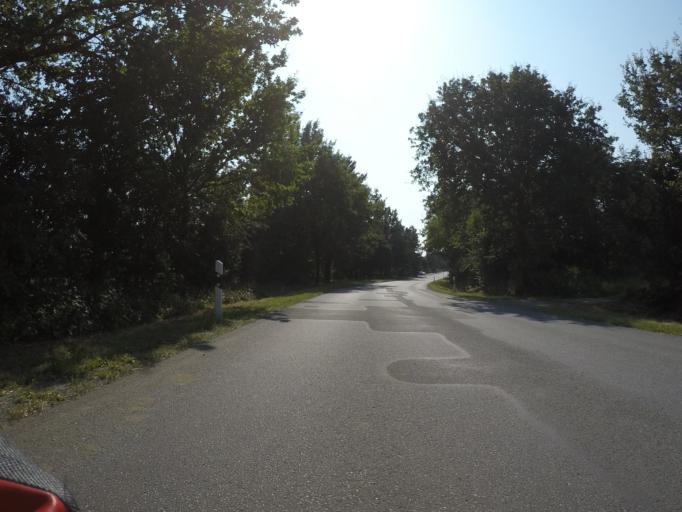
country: DE
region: Schleswig-Holstein
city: Bark
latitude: 53.9133
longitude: 10.1920
